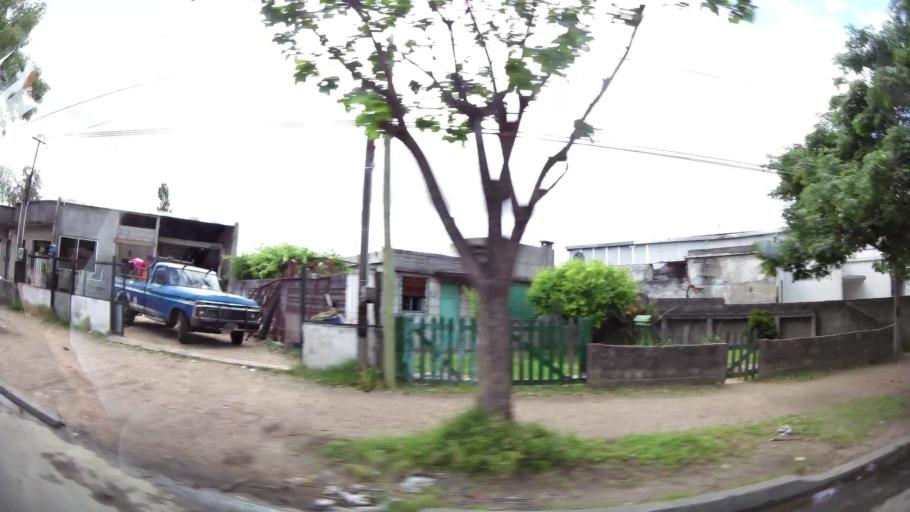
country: UY
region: Montevideo
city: Montevideo
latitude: -34.8343
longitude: -56.1453
